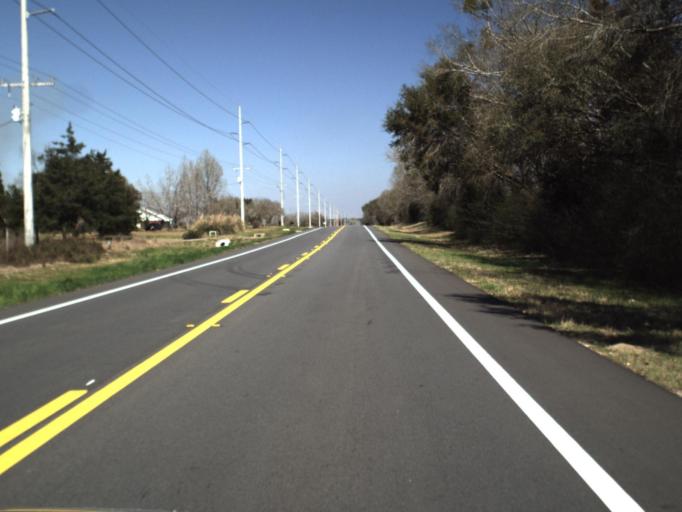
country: US
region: Florida
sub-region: Jackson County
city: Sneads
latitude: 30.7669
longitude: -85.0192
